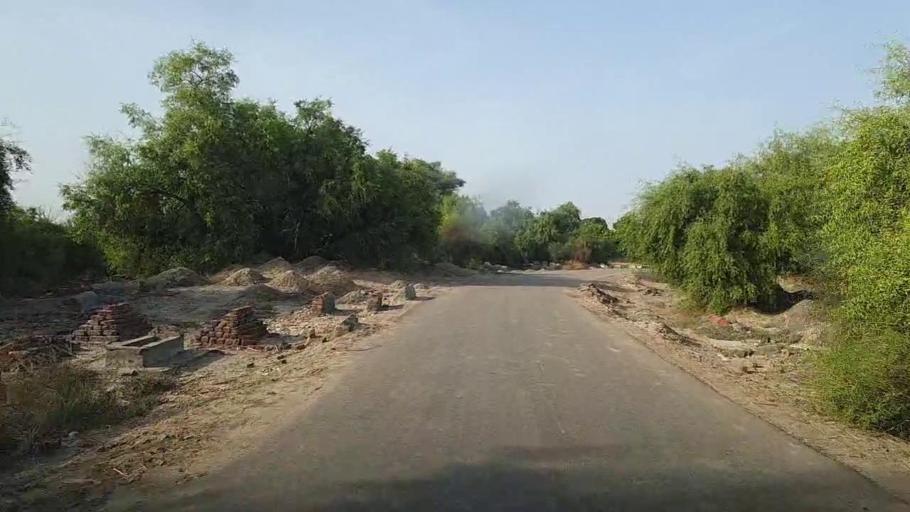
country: PK
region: Sindh
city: Ubauro
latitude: 28.1139
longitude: 69.8514
